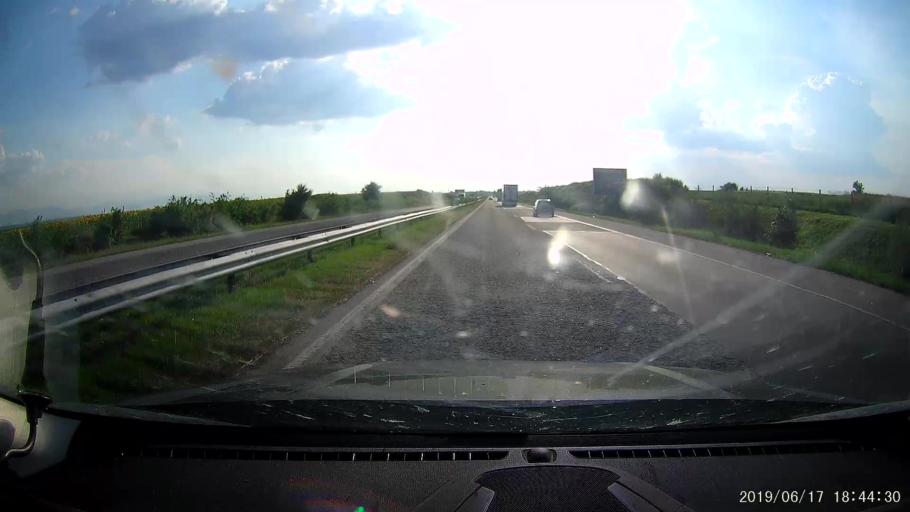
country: BG
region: Stara Zagora
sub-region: Obshtina Chirpan
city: Chirpan
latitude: 42.1930
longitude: 25.1798
